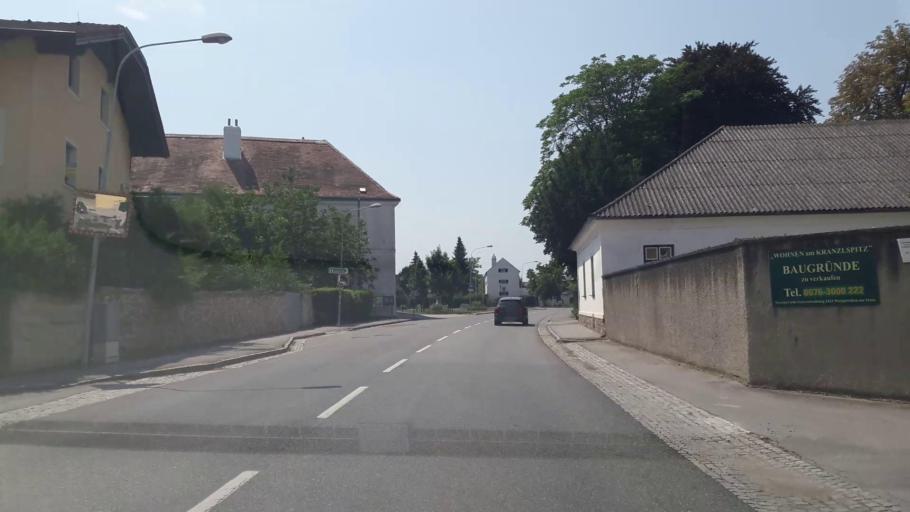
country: AT
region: Lower Austria
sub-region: Politischer Bezirk Wien-Umgebung
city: Schwadorf
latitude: 48.0506
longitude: 16.6068
